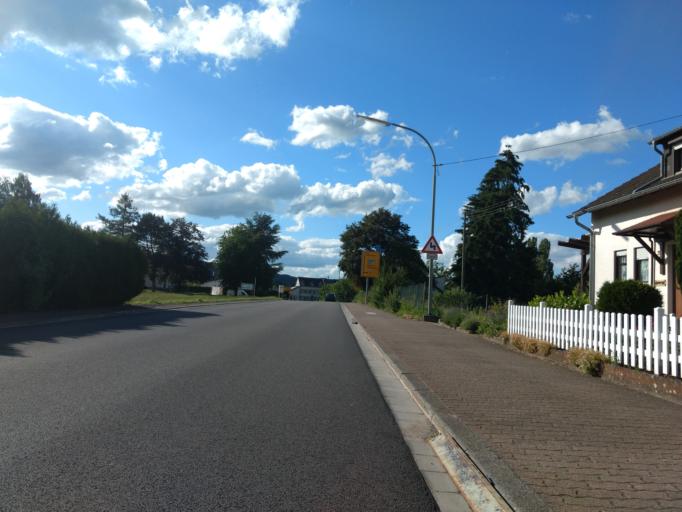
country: DE
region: Saarland
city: Merzig
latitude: 49.4542
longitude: 6.6014
